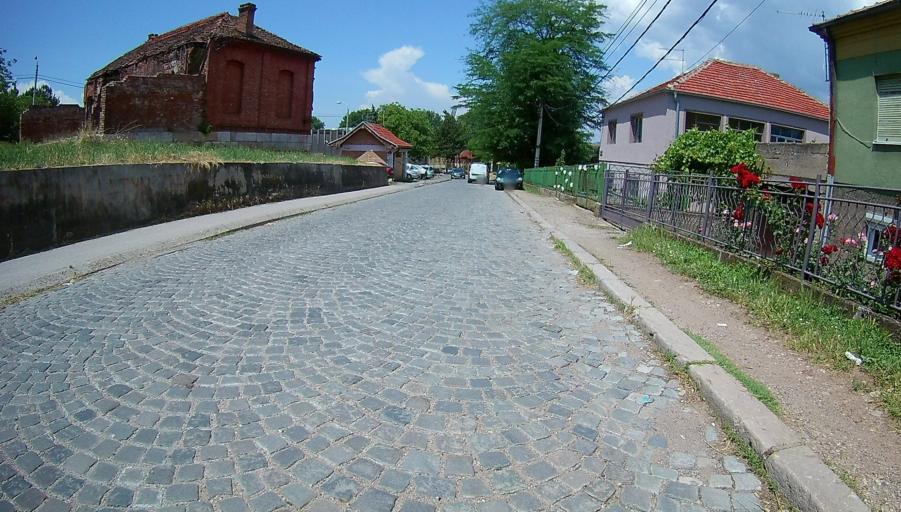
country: RS
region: Central Serbia
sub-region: Nisavski Okrug
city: Nis
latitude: 43.3107
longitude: 21.9119
